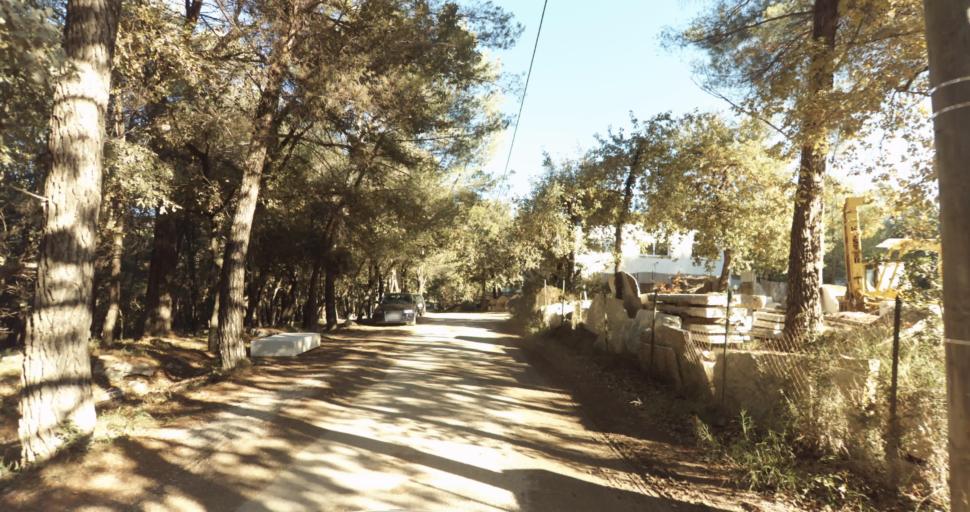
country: FR
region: Provence-Alpes-Cote d'Azur
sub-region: Departement des Alpes-Maritimes
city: La Colle-sur-Loup
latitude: 43.7111
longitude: 7.0856
